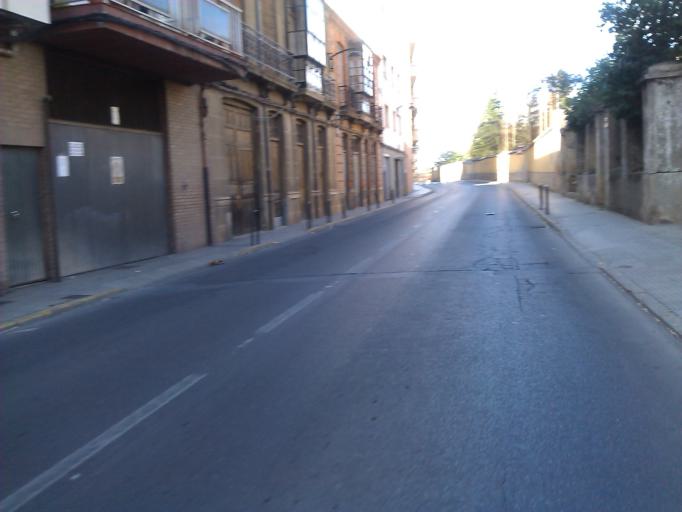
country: ES
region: Castille and Leon
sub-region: Provincia de Leon
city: Astorga
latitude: 42.4573
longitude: -6.0592
